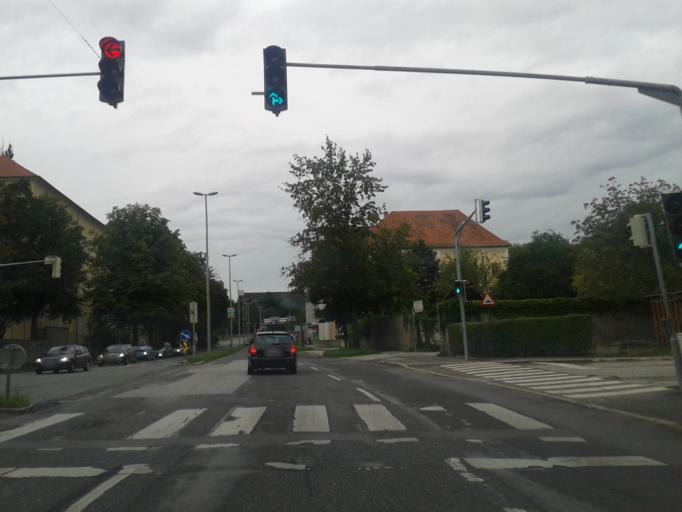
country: AT
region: Styria
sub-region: Graz Stadt
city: Goesting
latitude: 47.0851
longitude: 15.4184
